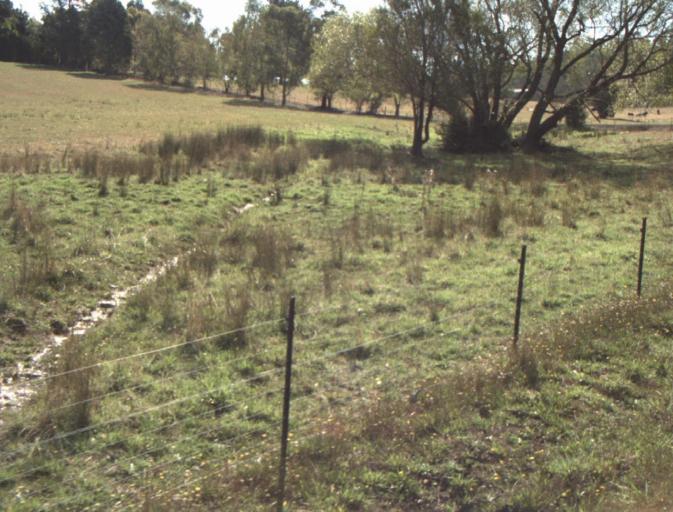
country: AU
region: Tasmania
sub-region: Launceston
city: Mayfield
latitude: -41.2371
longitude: 147.2340
